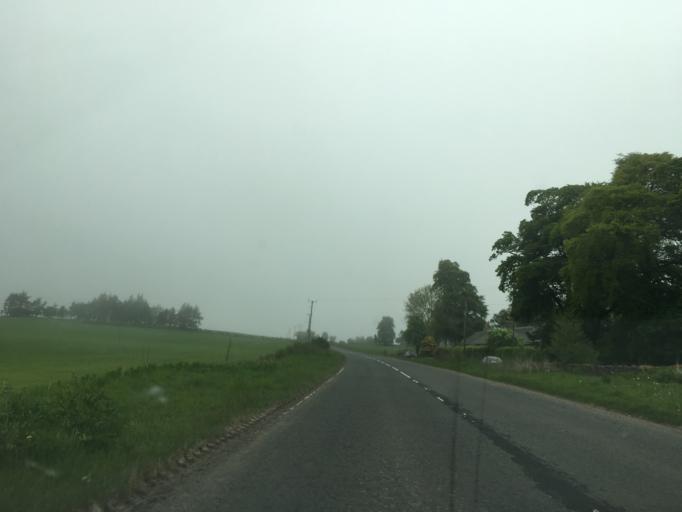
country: GB
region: Scotland
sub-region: The Scottish Borders
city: West Linton
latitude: 55.7397
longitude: -3.2987
